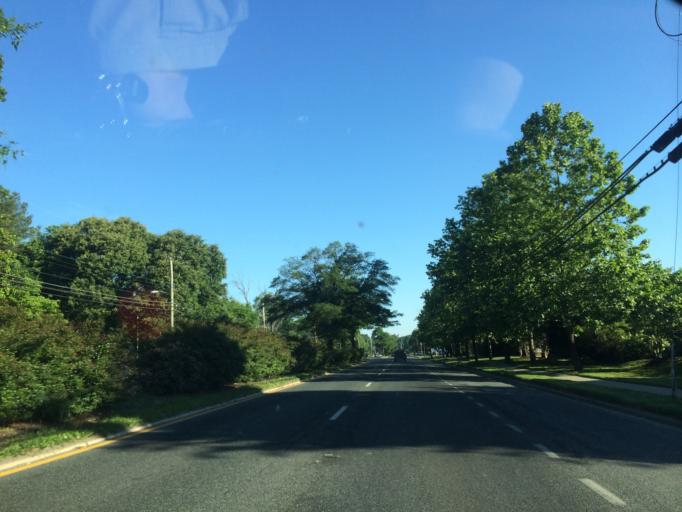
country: US
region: Maryland
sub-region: Wicomico County
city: Salisbury
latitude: 38.3720
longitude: -75.6156
